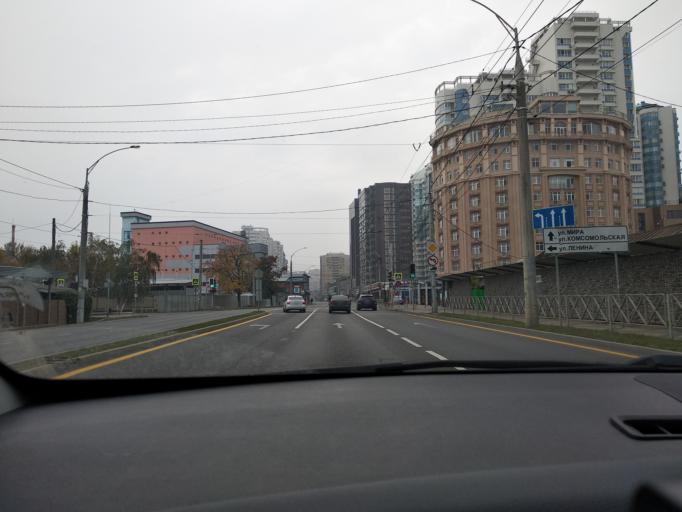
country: RU
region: Krasnodarskiy
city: Krasnodar
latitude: 45.0260
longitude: 38.9597
